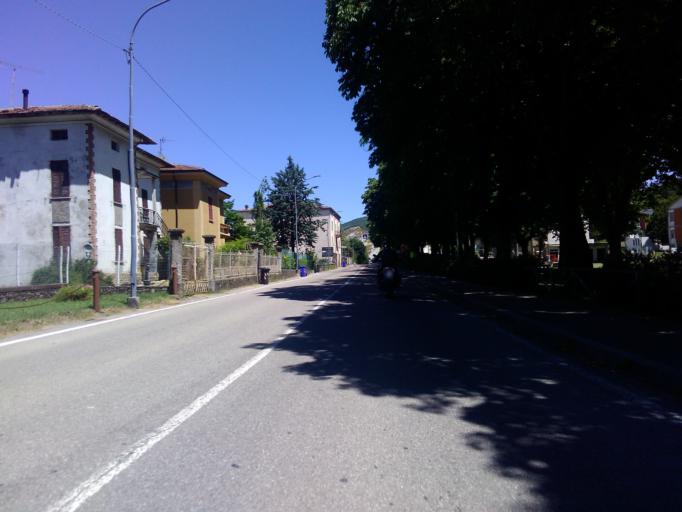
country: IT
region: Emilia-Romagna
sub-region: Provincia di Parma
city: Calestano
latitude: 44.6019
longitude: 10.1228
